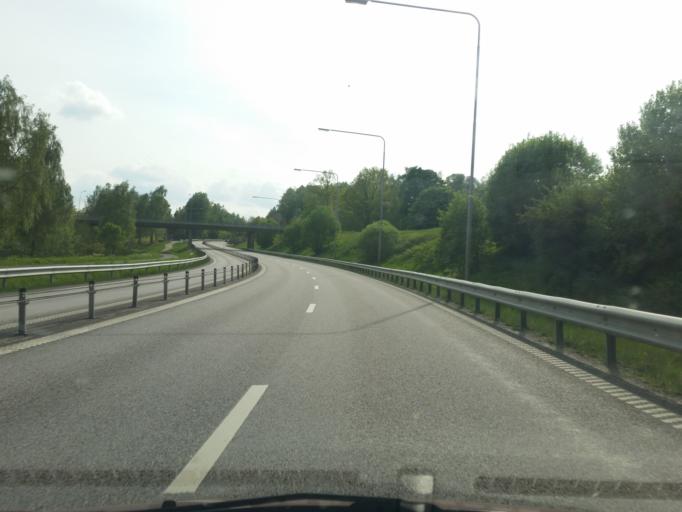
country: SE
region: Vaestra Goetaland
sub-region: Ulricehamns Kommun
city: Ulricehamn
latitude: 57.8030
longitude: 13.4012
